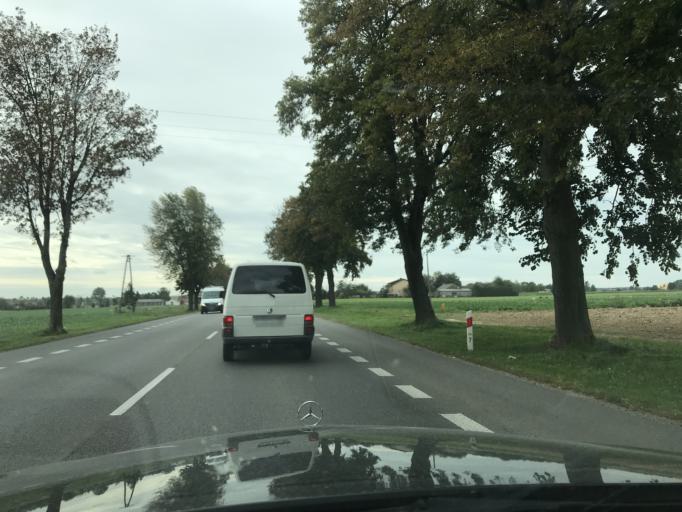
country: PL
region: Lublin Voivodeship
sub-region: Powiat lubelski
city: Niedrzwica Duza
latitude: 51.1597
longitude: 22.4082
